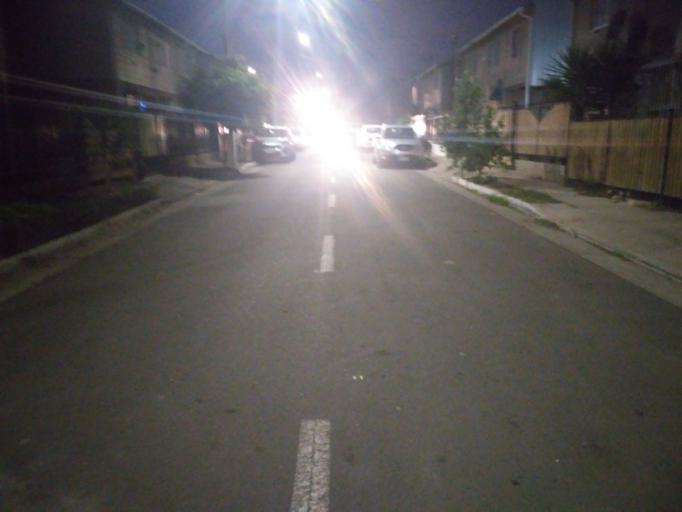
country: CL
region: Valparaiso
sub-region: Provincia de Quillota
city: Hacienda La Calera
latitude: -32.7947
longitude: -71.2230
